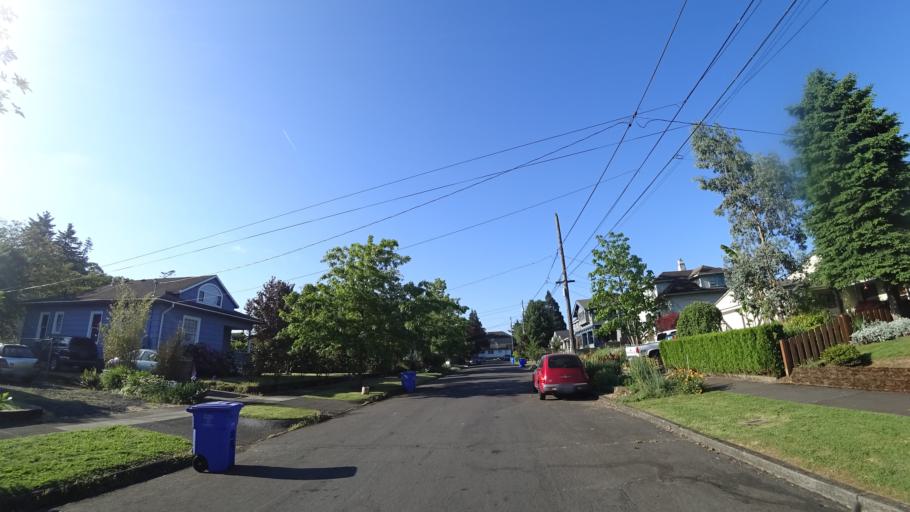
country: US
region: Oregon
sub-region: Multnomah County
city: Portland
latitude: 45.5637
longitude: -122.6470
